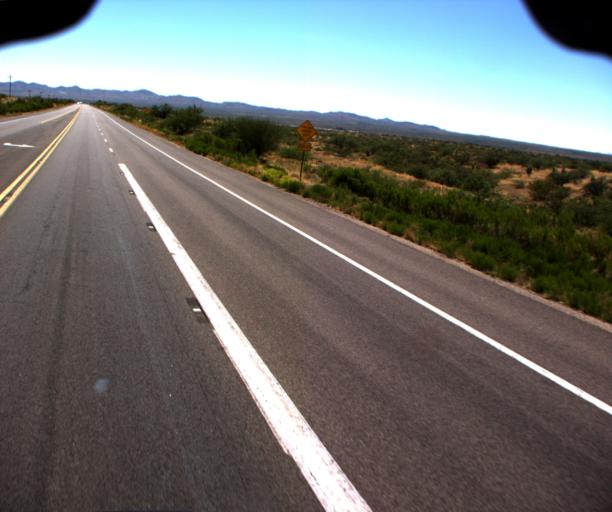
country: US
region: Arizona
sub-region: Pima County
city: Catalina
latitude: 32.5933
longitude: -110.8891
